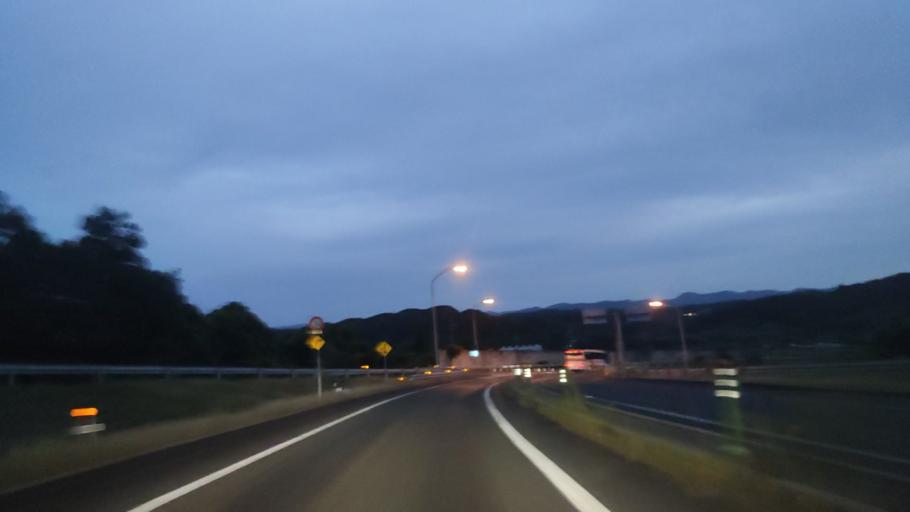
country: JP
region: Hyogo
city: Sandacho
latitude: 34.8894
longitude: 135.1173
